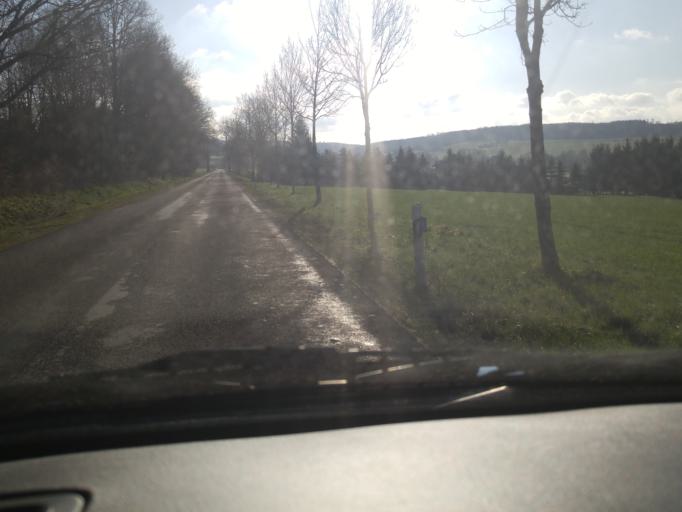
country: DE
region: Hesse
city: Herbstein
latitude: 50.5823
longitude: 9.3528
